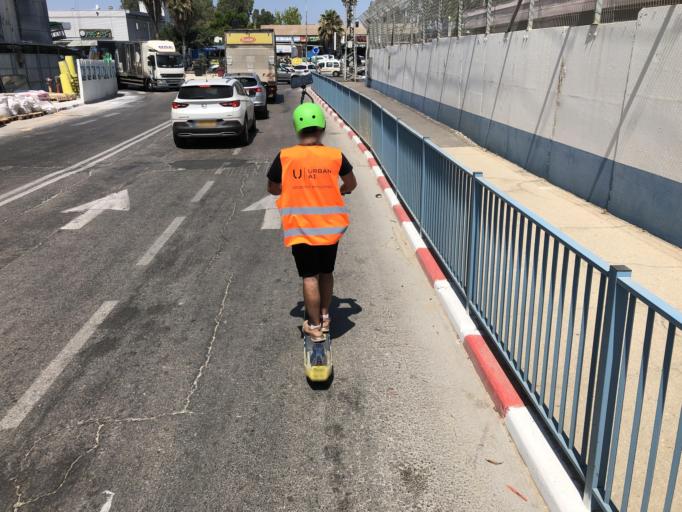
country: IL
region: Central District
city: Yehud
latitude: 32.0265
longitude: 34.8995
